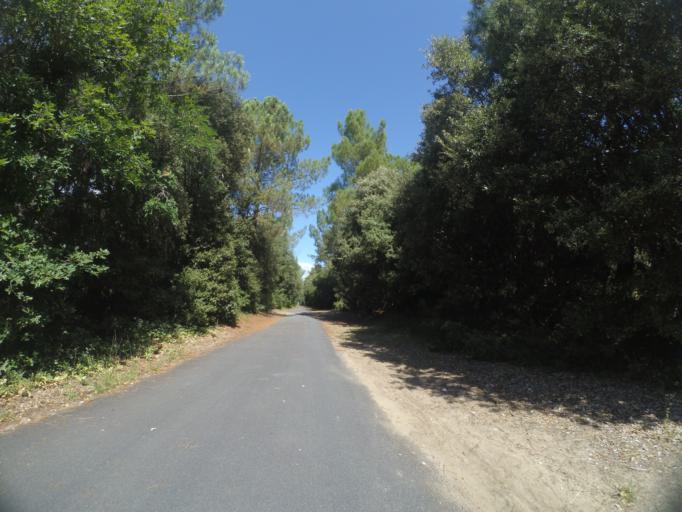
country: FR
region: Poitou-Charentes
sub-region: Departement de la Charente-Maritime
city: Les Mathes
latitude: 45.6743
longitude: -1.1504
